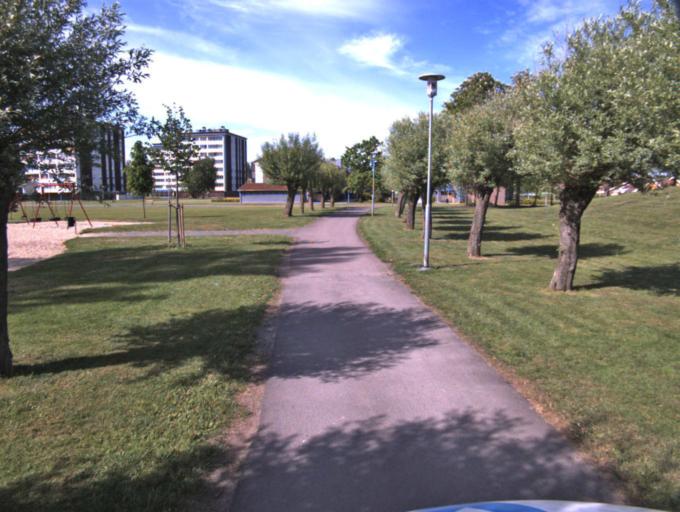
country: SE
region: Skane
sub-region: Kristianstads Kommun
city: Kristianstad
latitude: 56.0418
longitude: 14.1854
